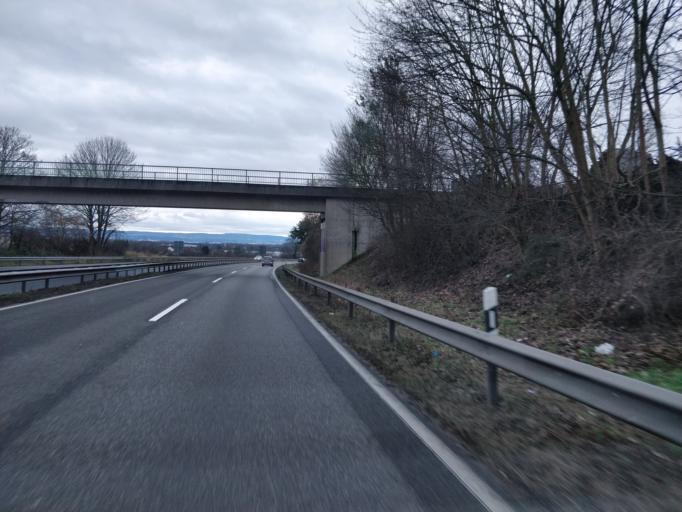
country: DE
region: Rheinland-Pfalz
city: Neuwied
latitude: 50.4528
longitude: 7.4845
